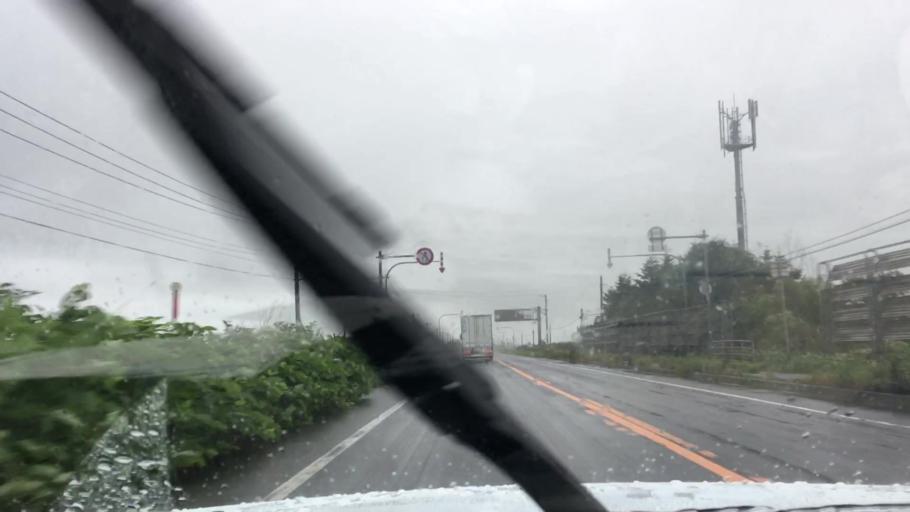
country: JP
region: Hokkaido
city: Niseko Town
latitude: 42.4314
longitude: 140.3185
